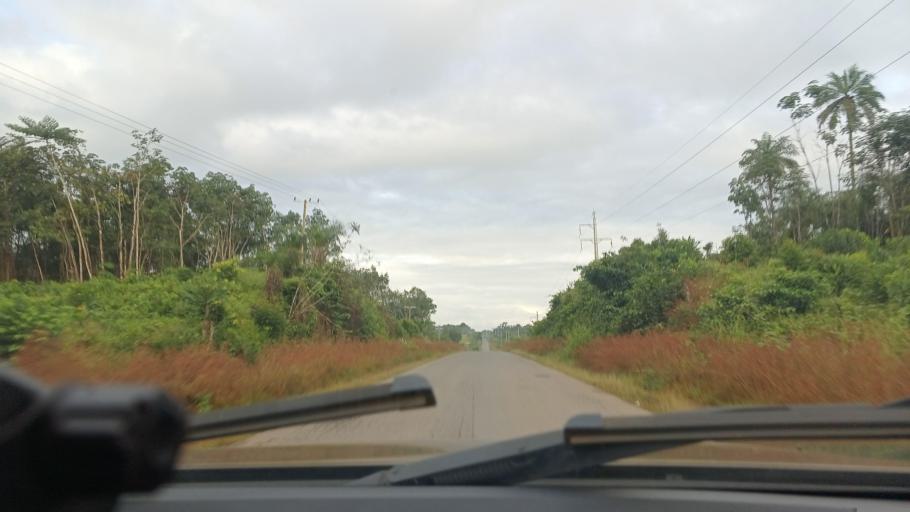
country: LR
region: Montserrado
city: Monrovia
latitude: 6.5450
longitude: -10.8596
